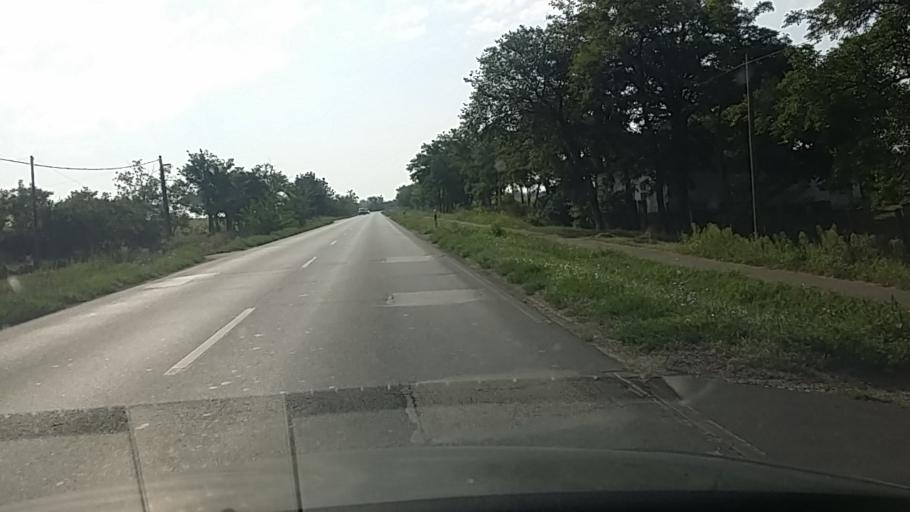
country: HU
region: Bekes
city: Kondoros
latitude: 46.7877
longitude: 20.7408
